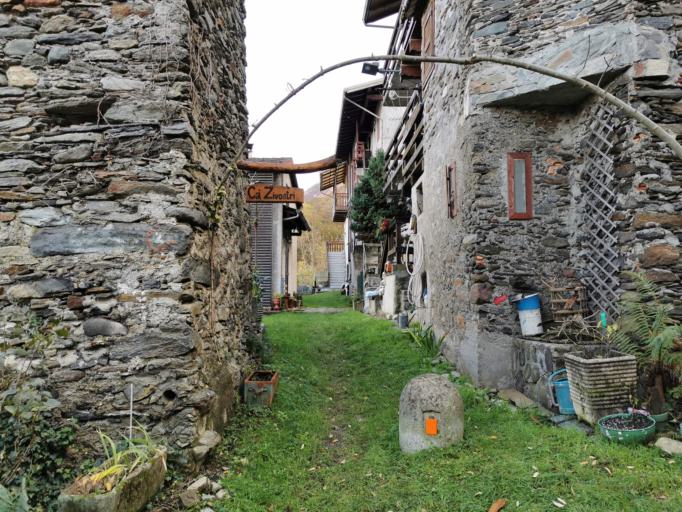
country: IT
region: Lombardy
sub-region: Provincia di Sondrio
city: Piantedo
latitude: 46.1286
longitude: 9.4393
